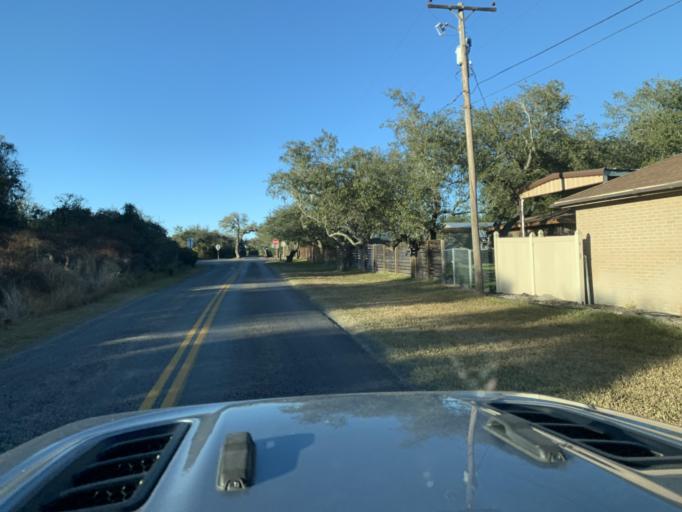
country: US
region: Texas
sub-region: Aransas County
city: Fulton
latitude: 28.1378
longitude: -96.9843
